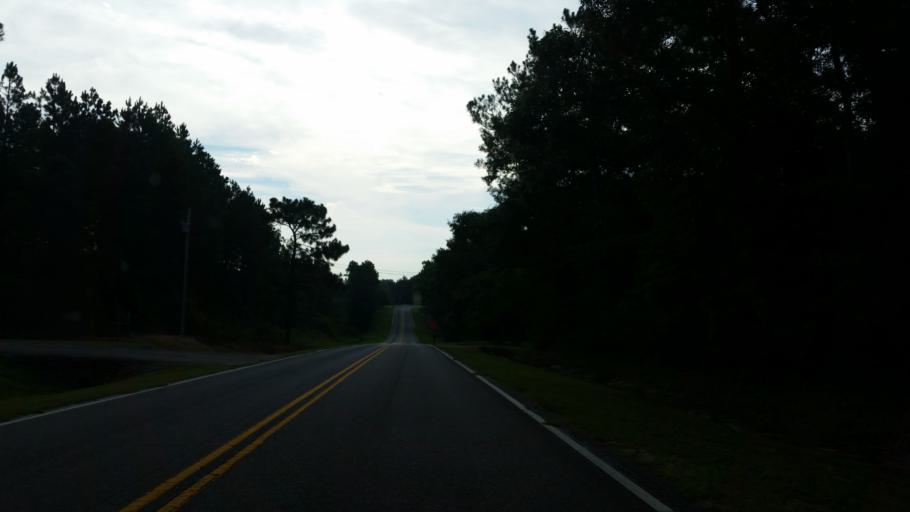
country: US
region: Florida
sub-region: Escambia County
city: Molino
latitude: 30.7739
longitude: -87.4825
